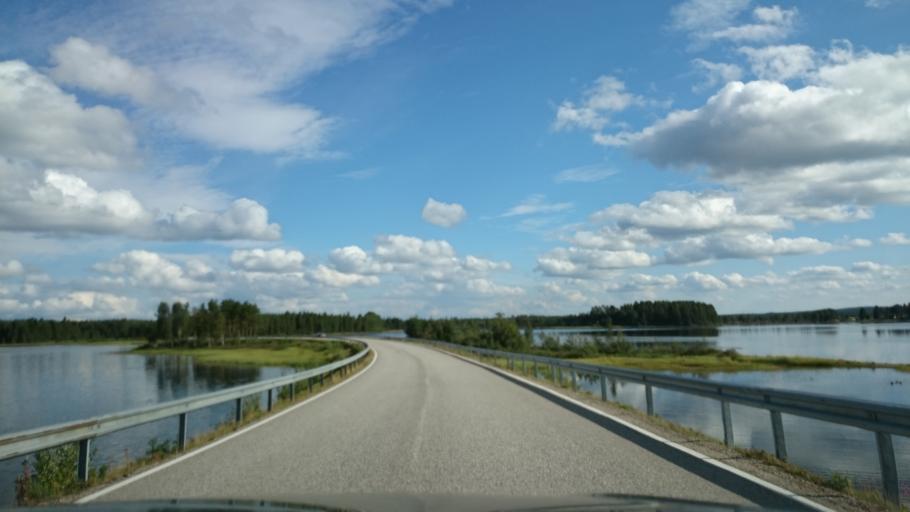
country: FI
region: Kainuu
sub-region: Kehys-Kainuu
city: Suomussalmi
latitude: 64.7628
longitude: 29.3736
